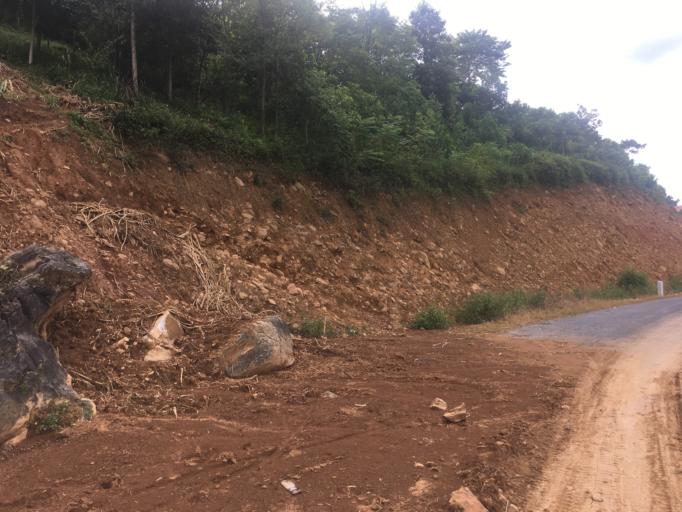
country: VN
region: Ha Giang
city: Thanh Pho Ha Giang
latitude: 22.9008
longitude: 105.0222
